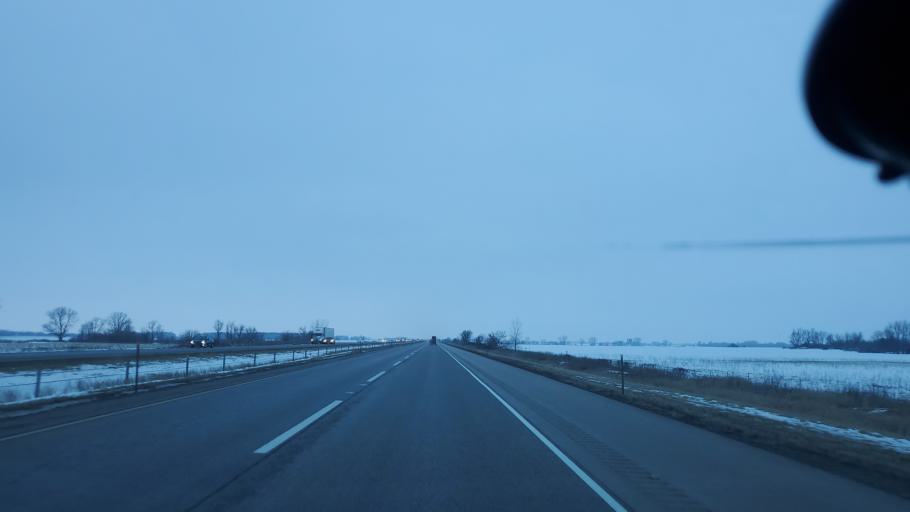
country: US
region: Illinois
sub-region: Kane County
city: Elburn
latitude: 41.8571
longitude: -88.5289
